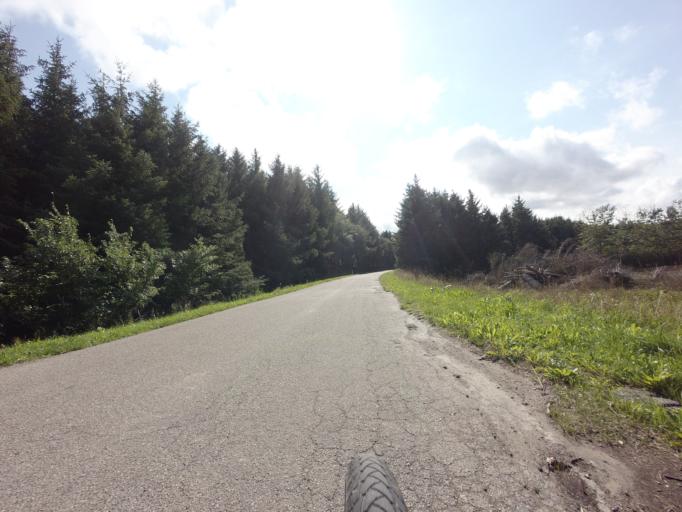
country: DK
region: North Denmark
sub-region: Hjorring Kommune
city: Hjorring
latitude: 57.5389
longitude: 10.0584
